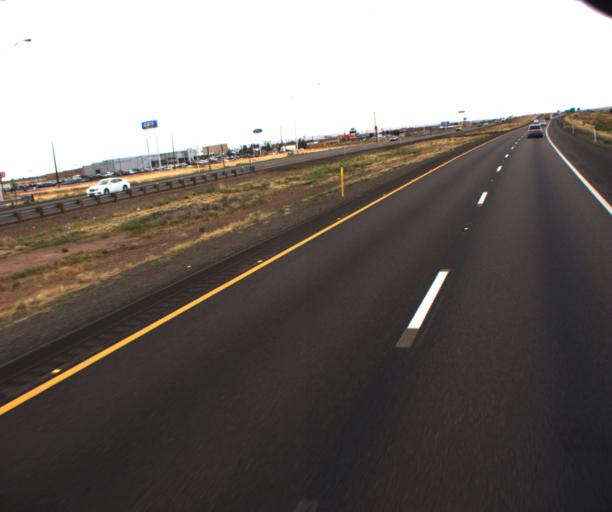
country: US
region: Arizona
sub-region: Navajo County
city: Winslow
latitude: 35.0392
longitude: -110.7076
